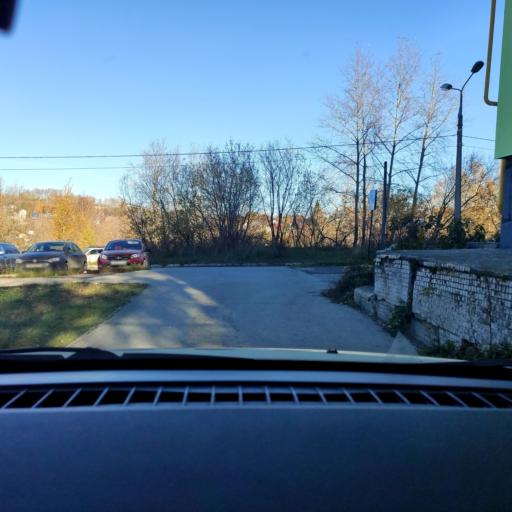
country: RU
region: Perm
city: Perm
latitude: 58.1132
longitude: 56.3774
